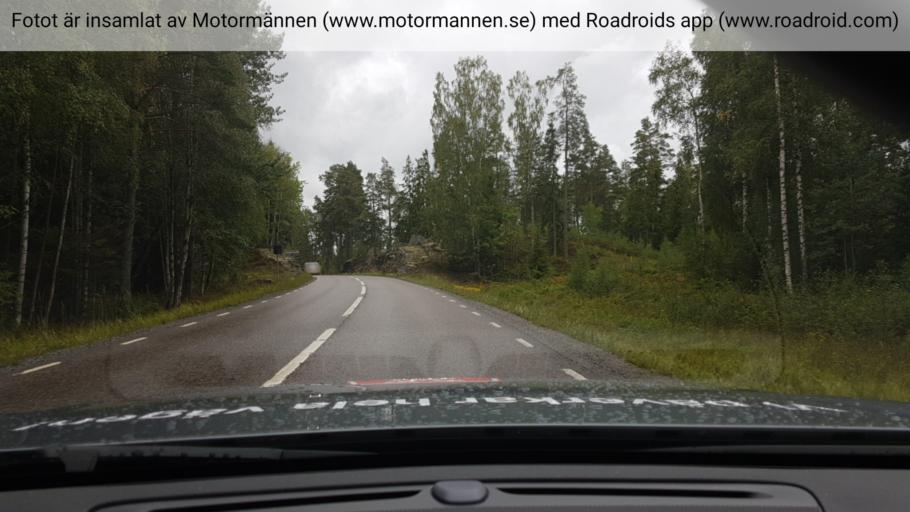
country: SE
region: Stockholm
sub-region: Botkyrka Kommun
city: Tullinge
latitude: 59.1798
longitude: 17.9283
